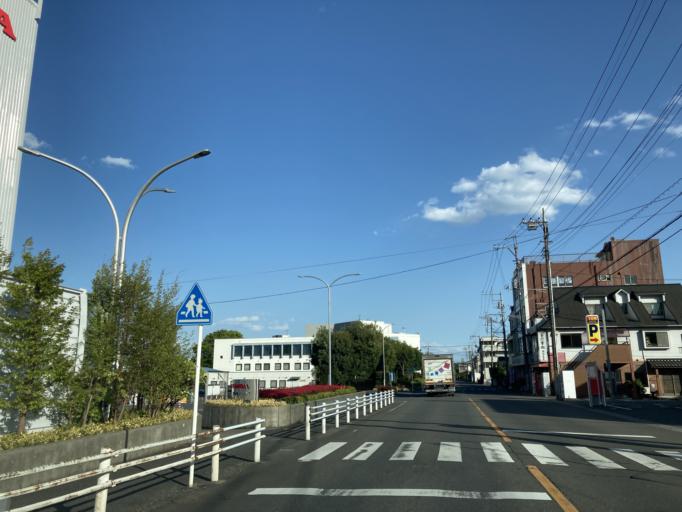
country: JP
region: Saitama
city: Sayama
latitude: 35.8745
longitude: 139.4373
